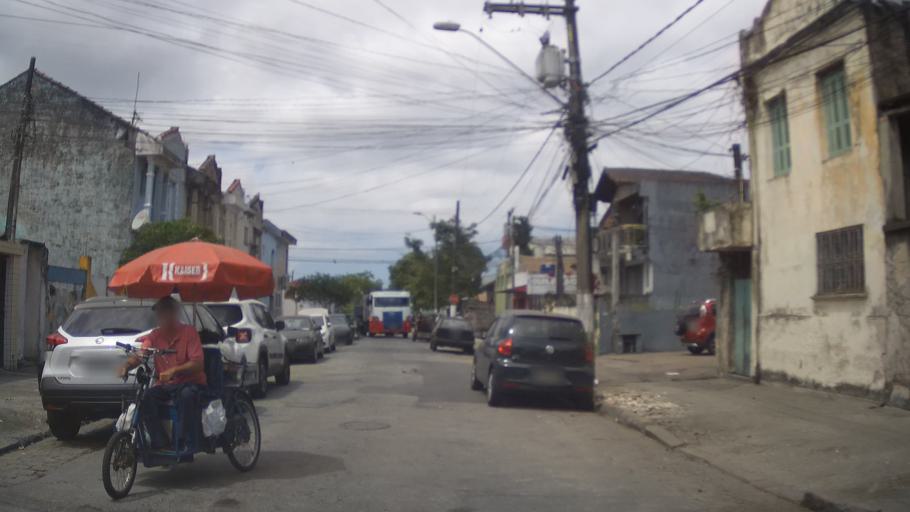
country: BR
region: Sao Paulo
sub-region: Santos
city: Santos
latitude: -23.9577
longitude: -46.3127
